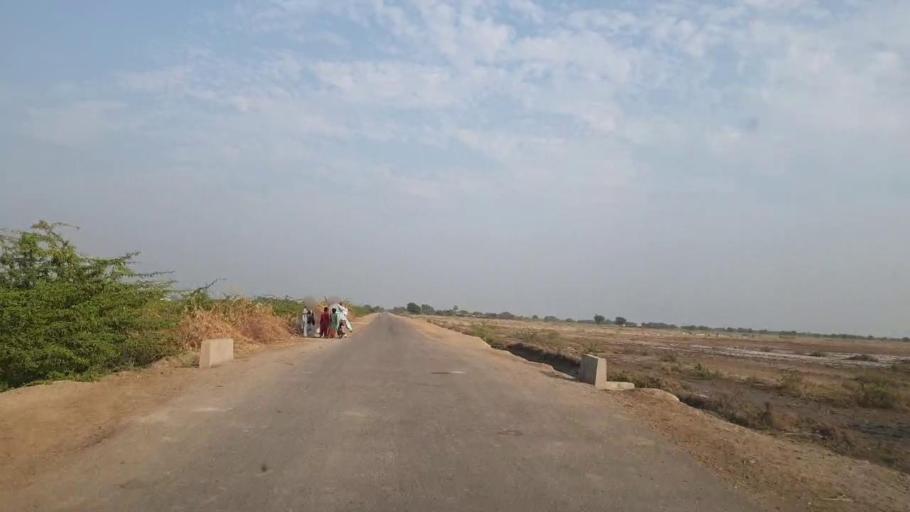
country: PK
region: Sindh
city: Pithoro
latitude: 25.5848
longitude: 69.3440
